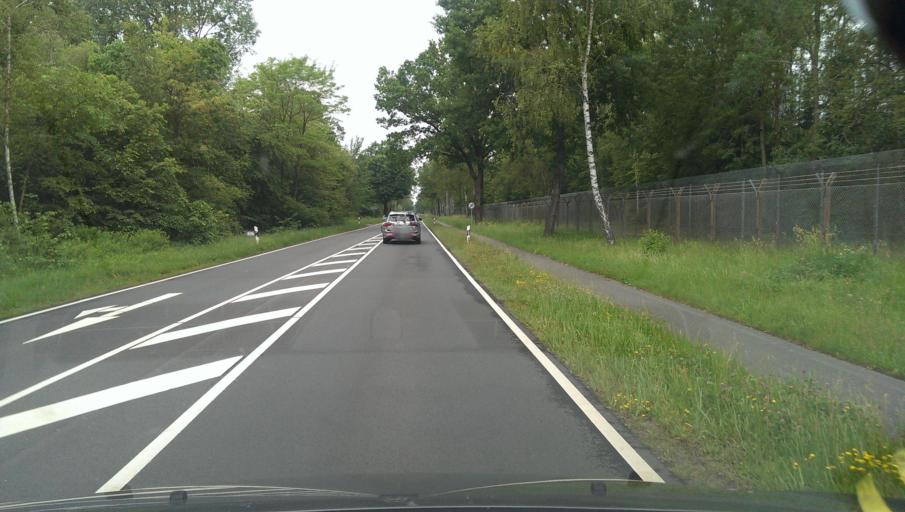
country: DE
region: Lower Saxony
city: Unterluss
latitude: 52.8544
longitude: 10.2836
